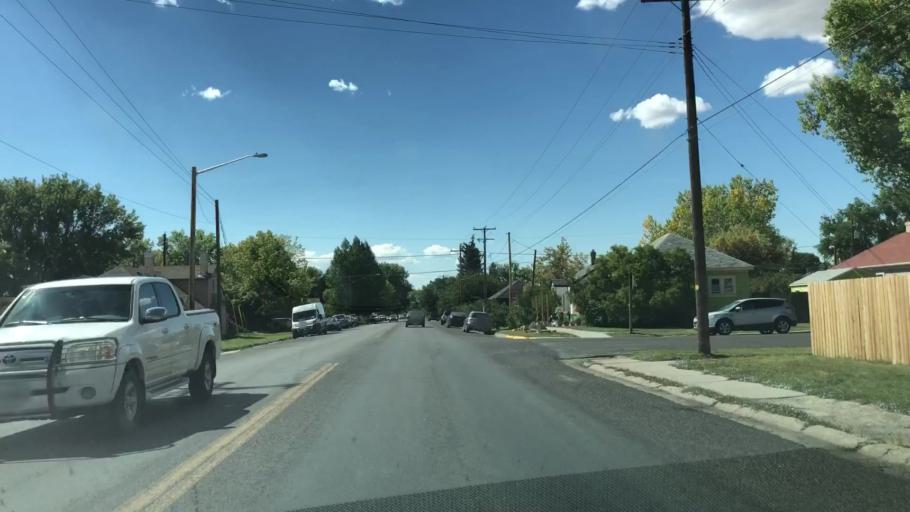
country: US
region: Wyoming
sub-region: Albany County
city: Laramie
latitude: 41.3031
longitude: -105.5875
